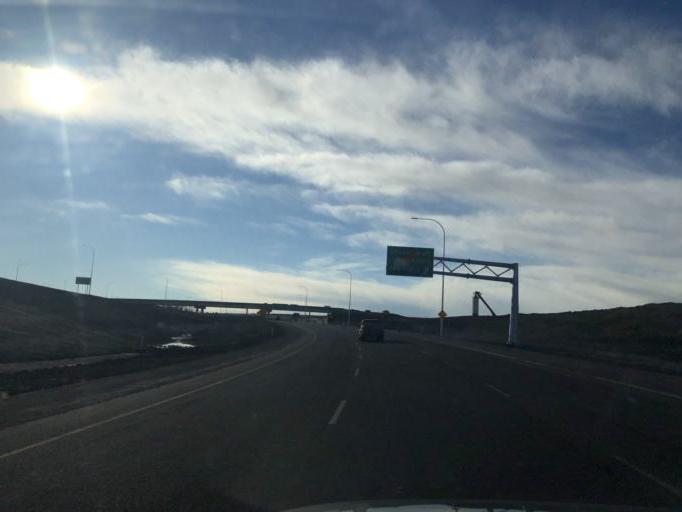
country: CA
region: Alberta
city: Calgary
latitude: 51.0044
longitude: -114.1672
